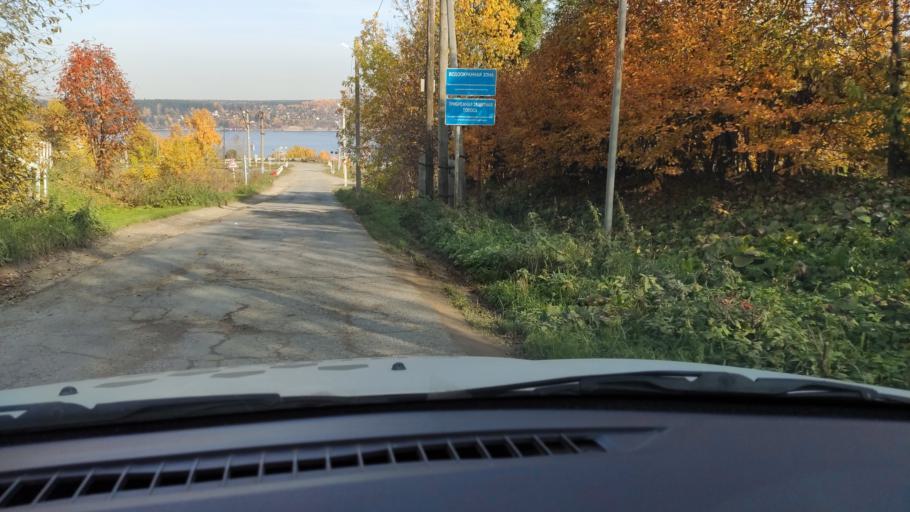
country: RU
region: Perm
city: Sylva
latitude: 58.0414
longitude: 56.7495
